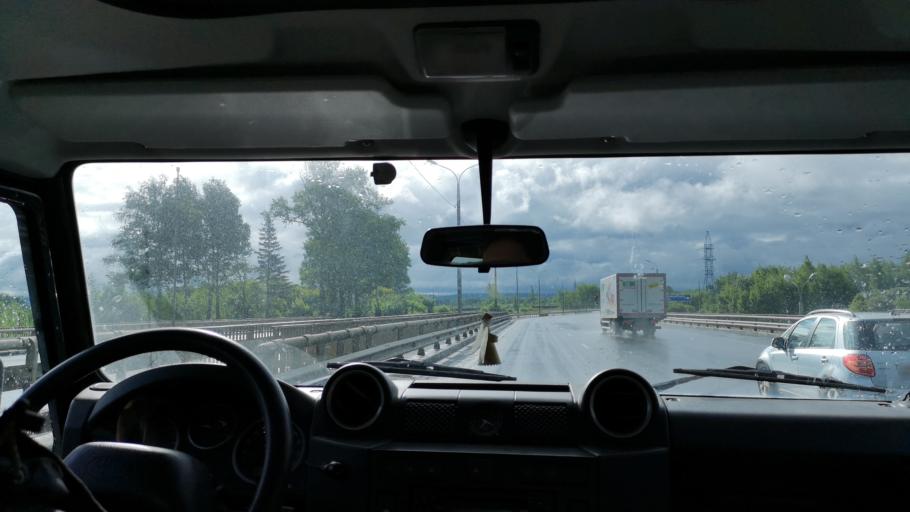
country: RU
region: Moskovskaya
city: Dmitrov
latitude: 56.3652
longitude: 37.4737
